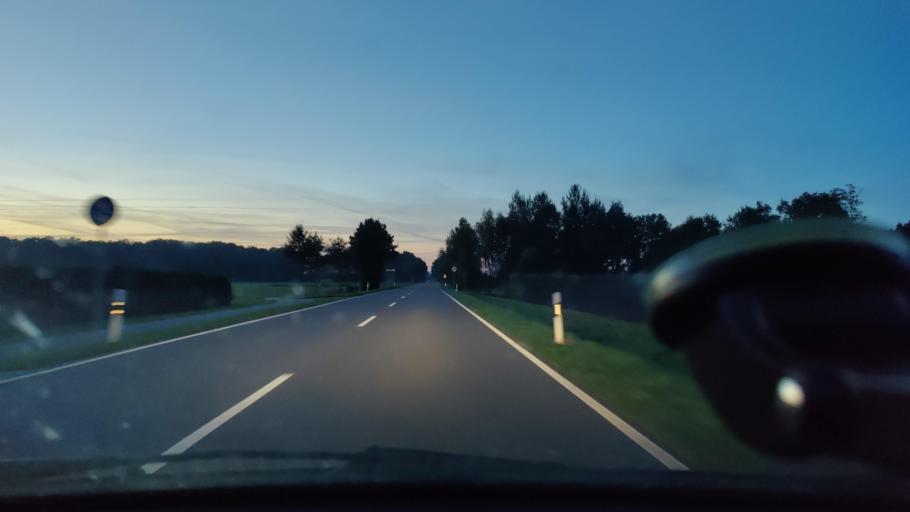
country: DE
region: North Rhine-Westphalia
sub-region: Regierungsbezirk Munster
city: Sudlohn
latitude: 51.8941
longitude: 6.8899
